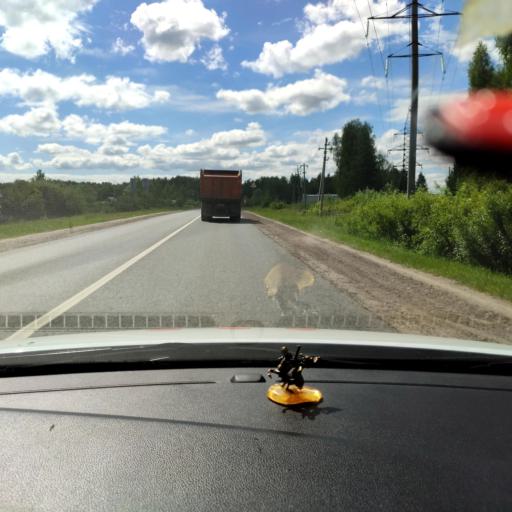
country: RU
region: Tatarstan
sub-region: Zelenodol'skiy Rayon
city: Vasil'yevo
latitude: 55.8535
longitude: 48.6679
